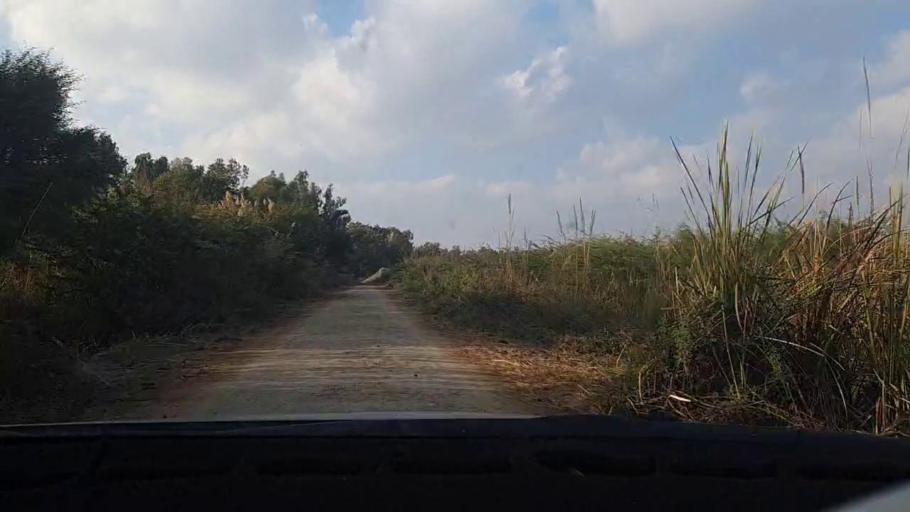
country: PK
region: Sindh
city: Tando Mittha Khan
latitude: 25.9114
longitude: 69.3043
